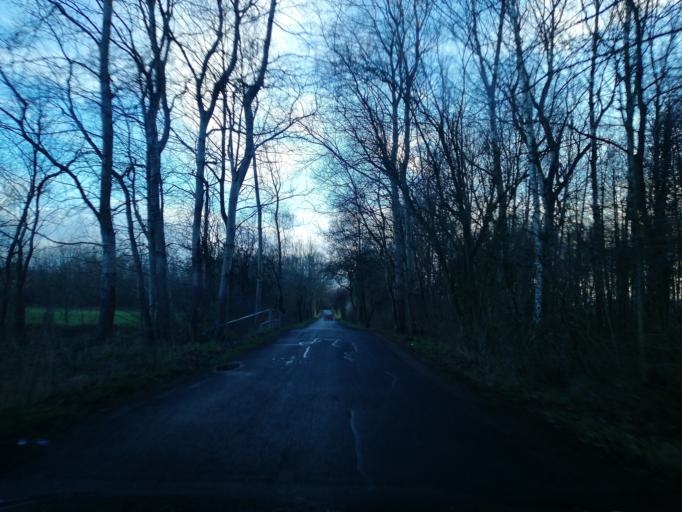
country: DE
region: Brandenburg
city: Calau
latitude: 51.7317
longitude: 13.9583
